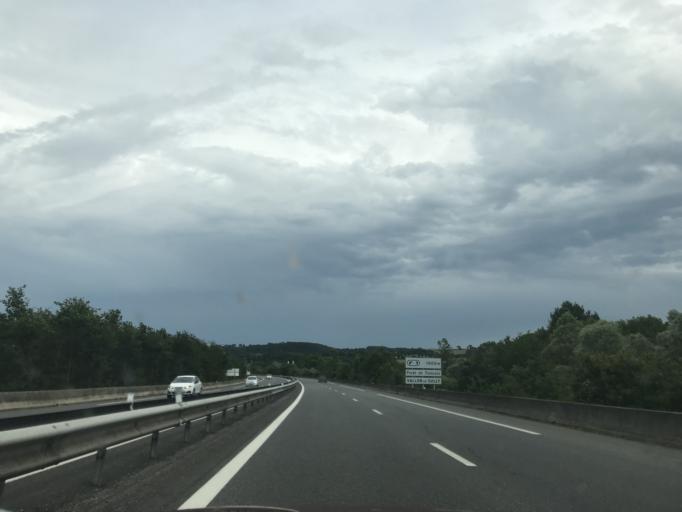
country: FR
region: Auvergne
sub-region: Departement de l'Allier
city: Vallon-en-Sully
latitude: 46.5083
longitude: 2.6127
